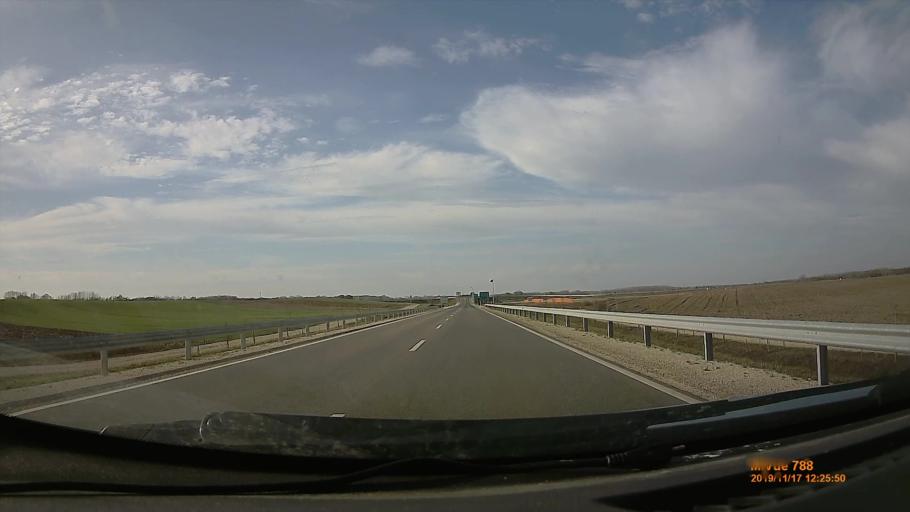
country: HU
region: Bacs-Kiskun
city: Kecskemet
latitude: 46.9315
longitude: 19.6271
